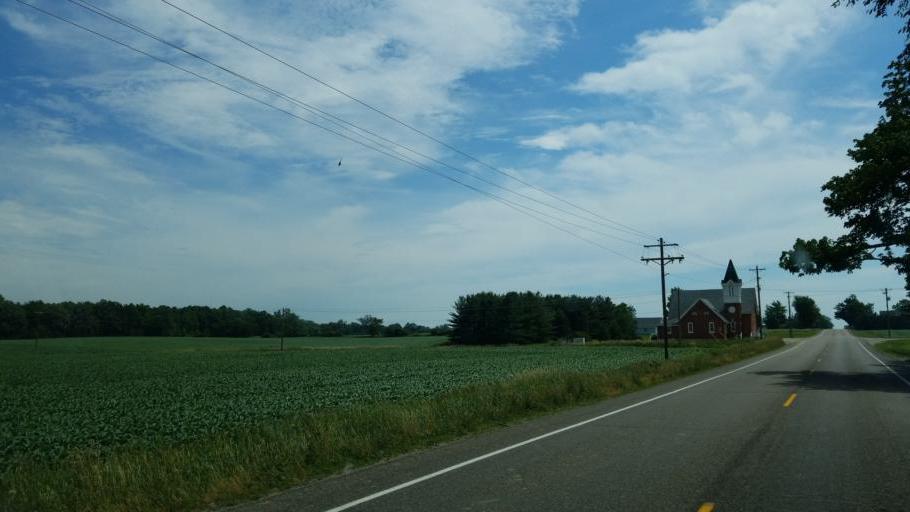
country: US
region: Michigan
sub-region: Eaton County
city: Charlotte
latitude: 42.6260
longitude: -84.8191
